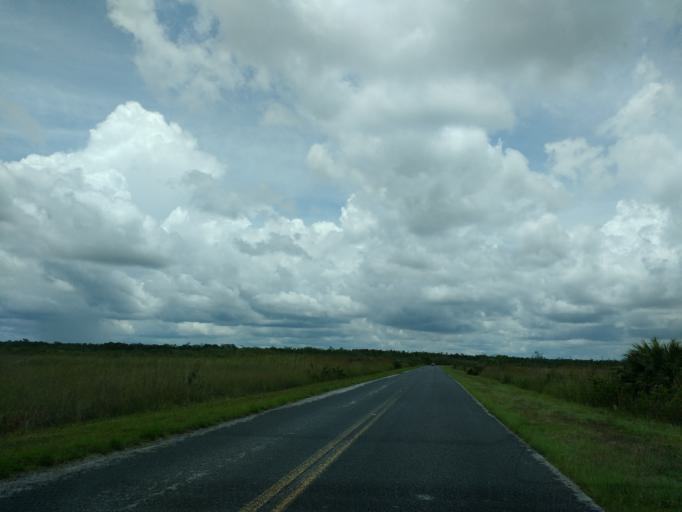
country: US
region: Florida
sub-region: Miami-Dade County
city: Florida City
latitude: 25.3882
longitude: -80.6129
